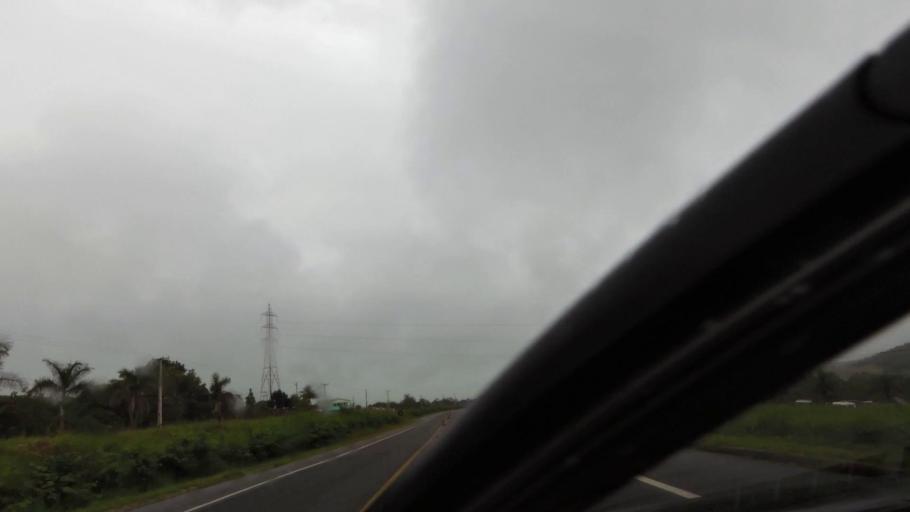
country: BR
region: Espirito Santo
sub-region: Guarapari
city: Guarapari
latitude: -20.7260
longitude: -40.5649
